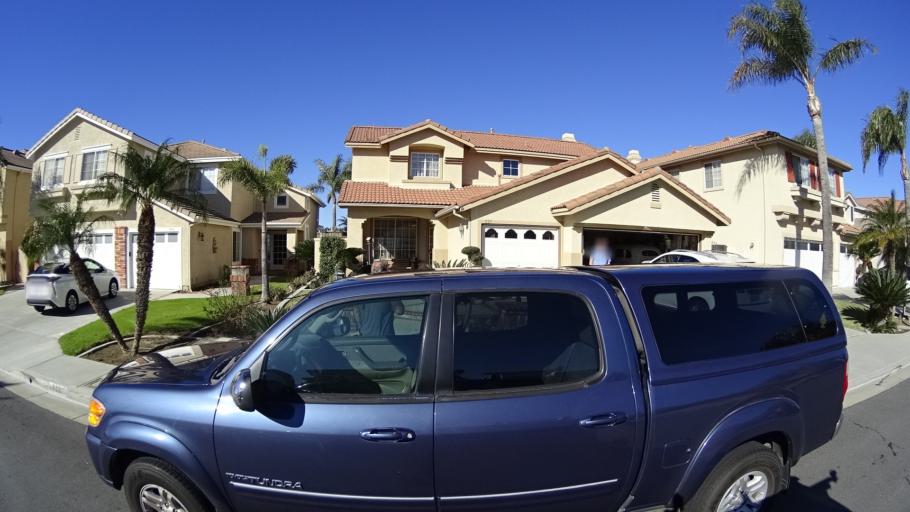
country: US
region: California
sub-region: Orange County
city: Yorba Linda
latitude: 33.8526
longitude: -117.7491
